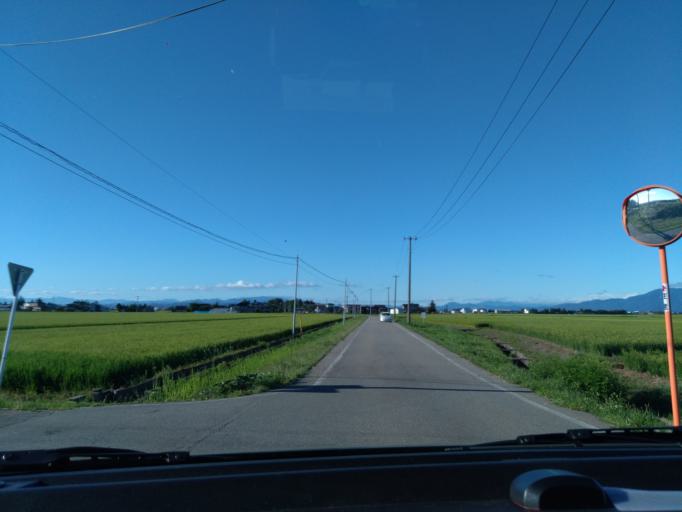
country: JP
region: Akita
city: Omagari
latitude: 39.4137
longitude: 140.5144
